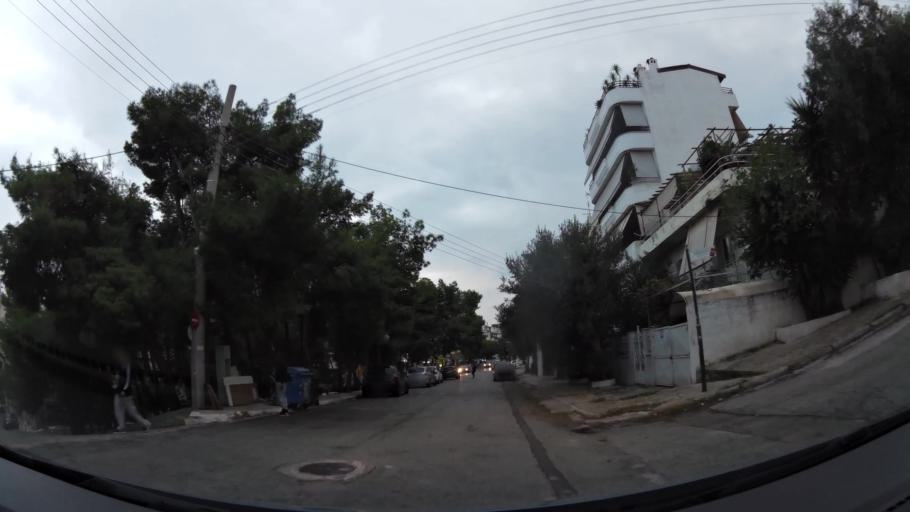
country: GR
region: Attica
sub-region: Nomarchia Athinas
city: Agios Dimitrios
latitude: 37.9376
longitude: 23.7448
